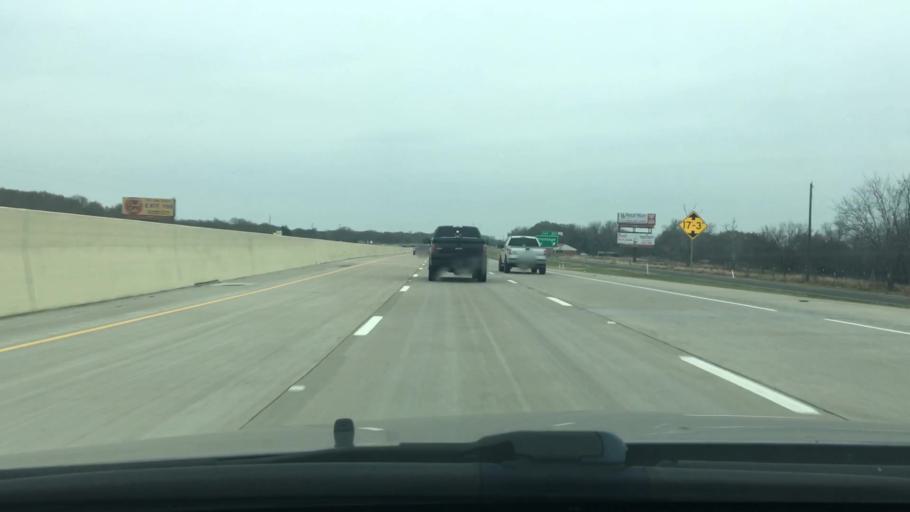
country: US
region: Texas
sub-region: Navarro County
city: Corsicana
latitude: 31.9699
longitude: -96.4221
